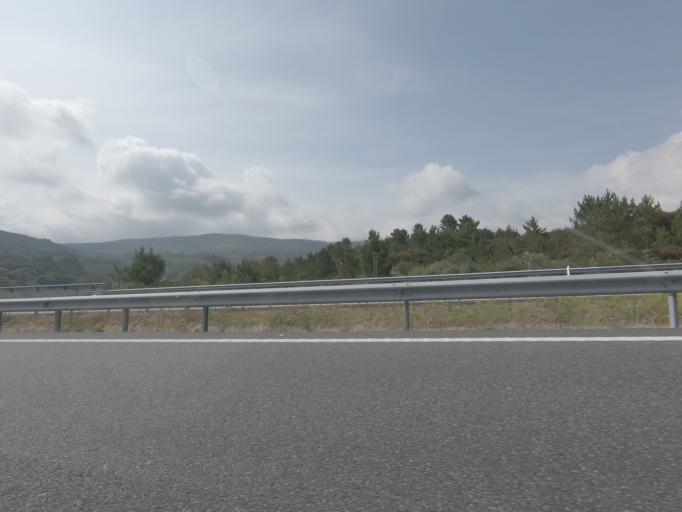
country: ES
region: Galicia
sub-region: Provincia de Pontevedra
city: Covelo
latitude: 42.1968
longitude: -8.3044
